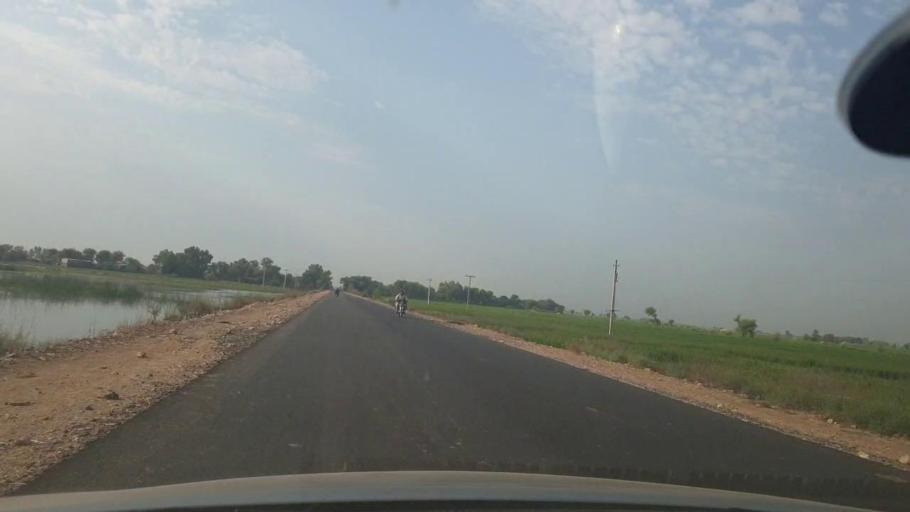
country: PK
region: Sindh
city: Jacobabad
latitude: 28.1150
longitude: 68.3269
